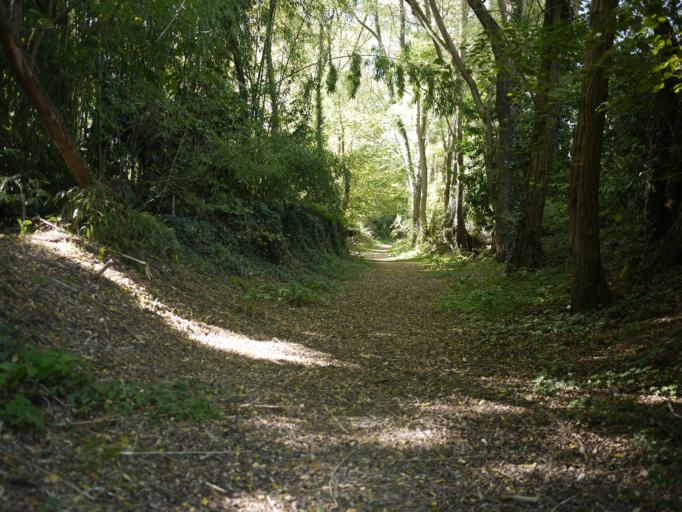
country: FR
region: Aquitaine
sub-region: Departement des Landes
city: Saint-Paul-les-Dax
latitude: 43.7243
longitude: -1.0728
